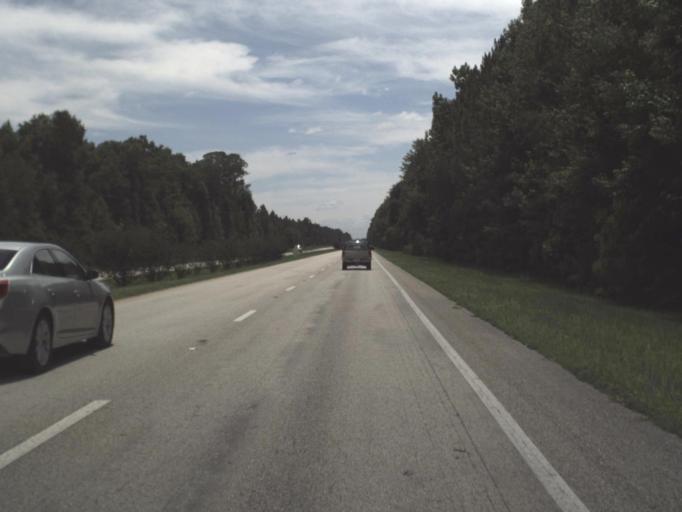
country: US
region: Florida
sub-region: Nassau County
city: Nassau Village-Ratliff
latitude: 30.4703
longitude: -81.7788
